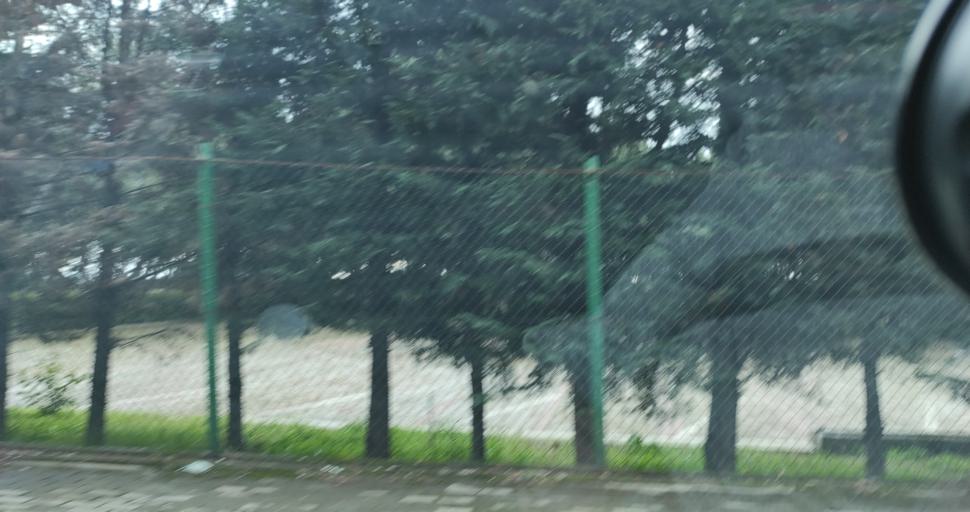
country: AL
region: Lezhe
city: Shengjin
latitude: 41.8194
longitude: 19.5649
